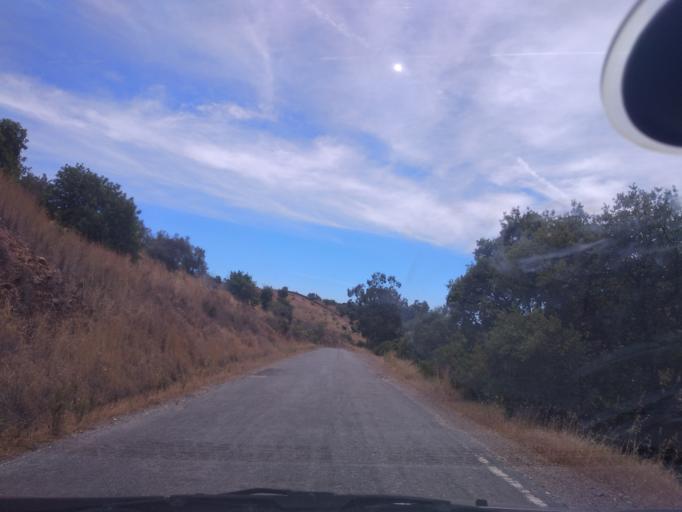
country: PT
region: Faro
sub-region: Olhao
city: Moncarapacho
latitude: 37.1685
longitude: -7.8035
